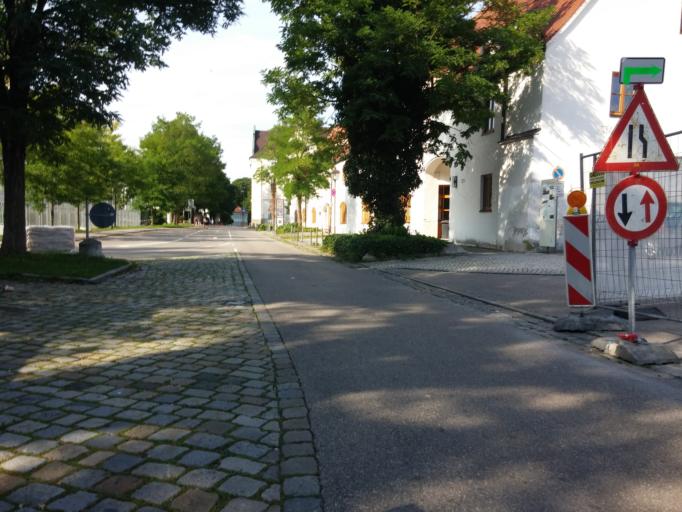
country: DE
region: Bavaria
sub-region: Upper Bavaria
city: Landsberg am Lech
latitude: 48.0508
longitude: 10.8742
